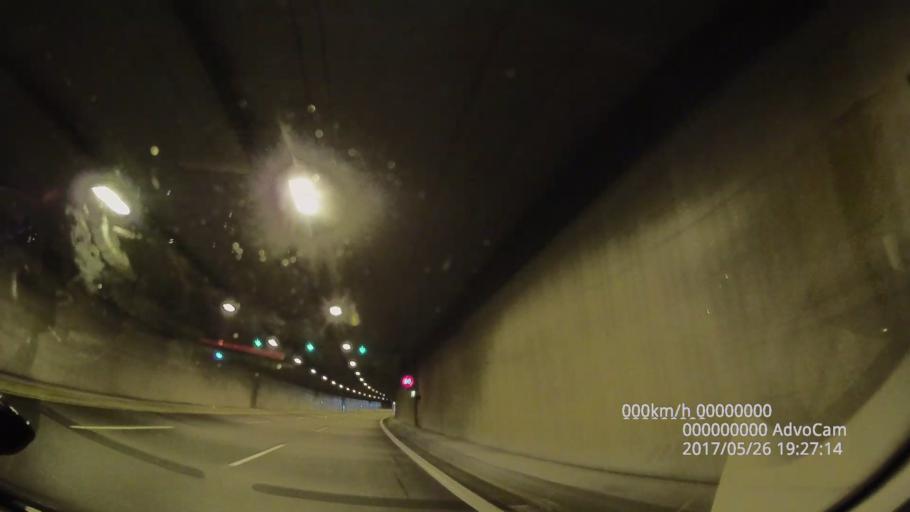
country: GR
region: Central Macedonia
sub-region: Nomos Thessalonikis
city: Nea Malgara
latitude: 40.5947
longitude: 22.6666
